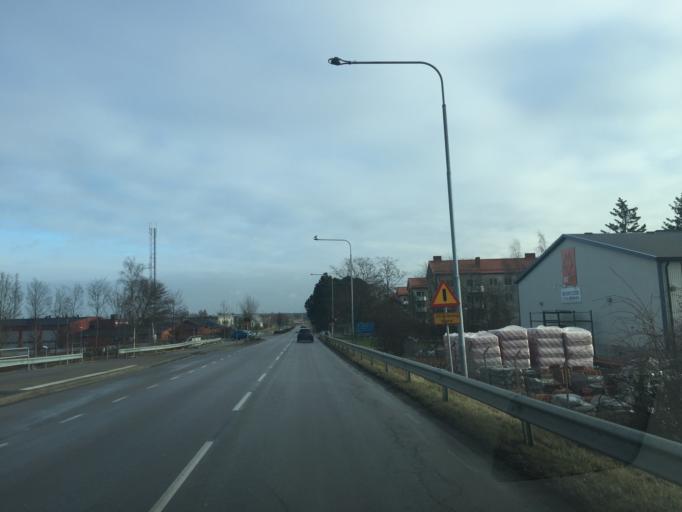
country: SE
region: Skane
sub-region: Svedala Kommun
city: Svedala
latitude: 55.5156
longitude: 13.2365
